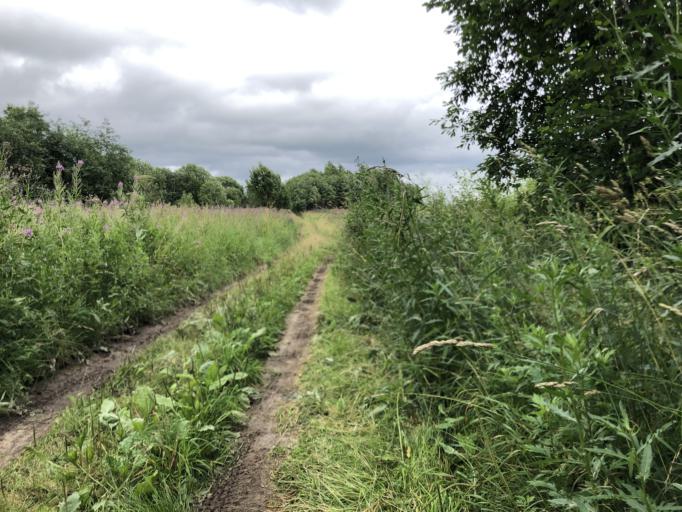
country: RU
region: Tverskaya
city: Rzhev
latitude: 56.2385
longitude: 34.3826
